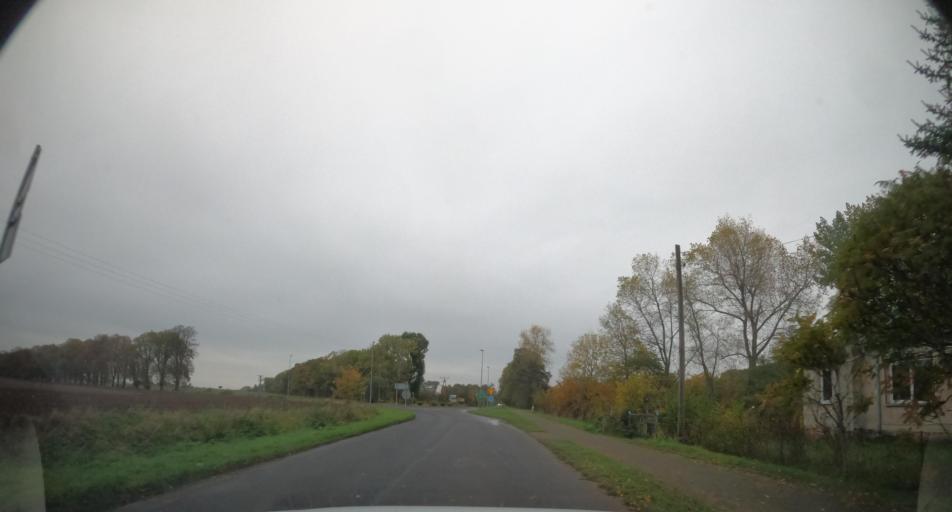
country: PL
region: West Pomeranian Voivodeship
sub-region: Powiat kamienski
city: Wolin
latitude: 53.8965
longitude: 14.6316
